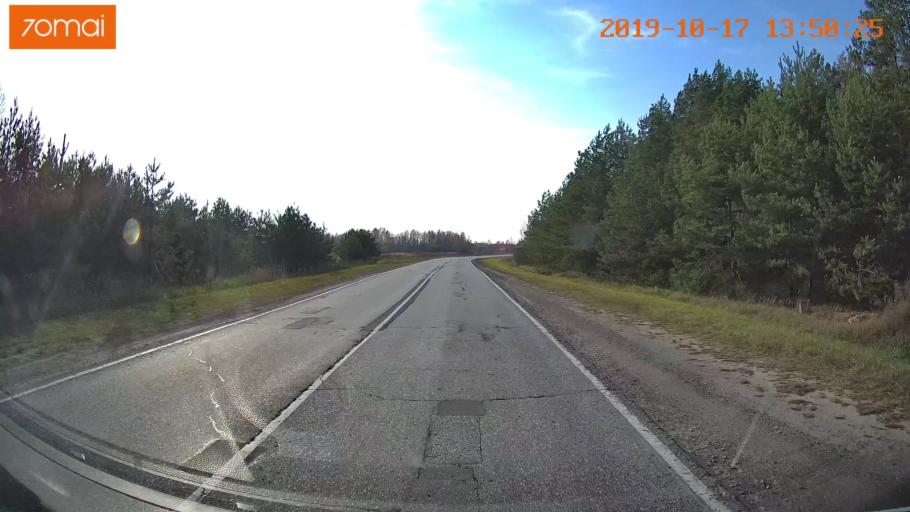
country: RU
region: Rjazan
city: Tuma
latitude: 55.1411
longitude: 40.4075
